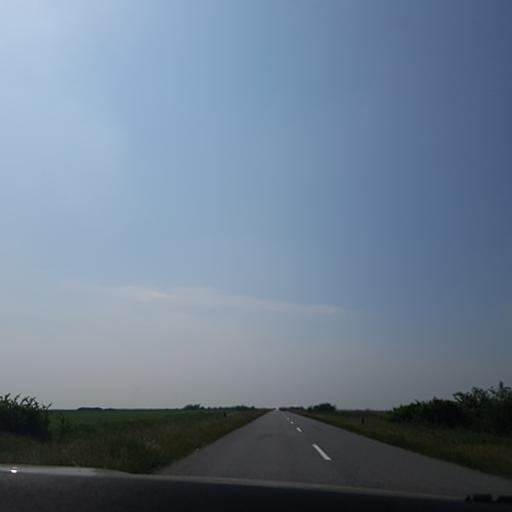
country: RS
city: Neuzina
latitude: 45.3358
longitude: 20.7242
